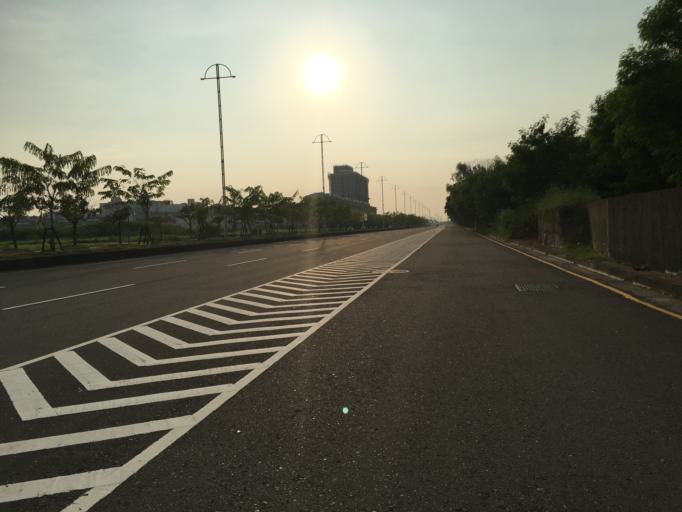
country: TW
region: Taiwan
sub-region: Chiayi
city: Taibao
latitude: 23.4687
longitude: 120.3000
